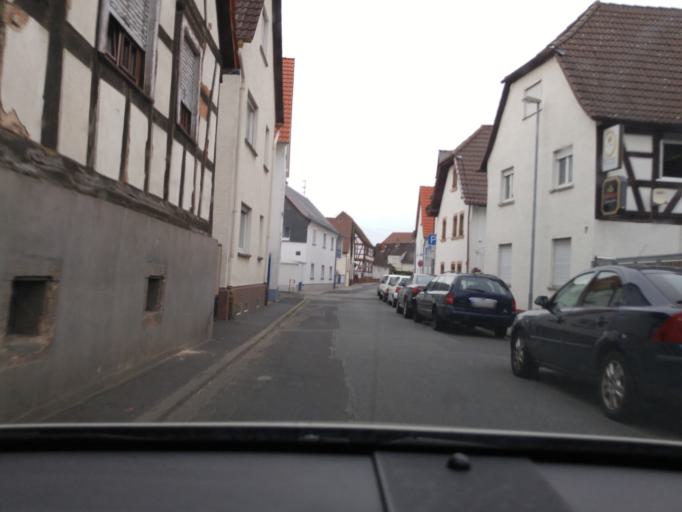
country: DE
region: Hesse
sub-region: Regierungsbezirk Darmstadt
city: Egelsbach
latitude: 49.9703
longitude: 8.6680
